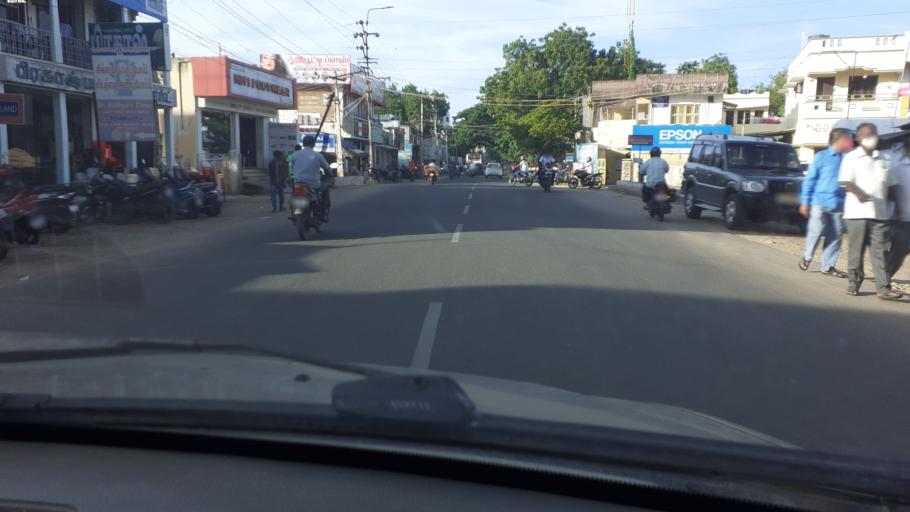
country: IN
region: Tamil Nadu
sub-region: Tirunelveli Kattabo
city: Tirunelveli
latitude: 8.7221
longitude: 77.7321
